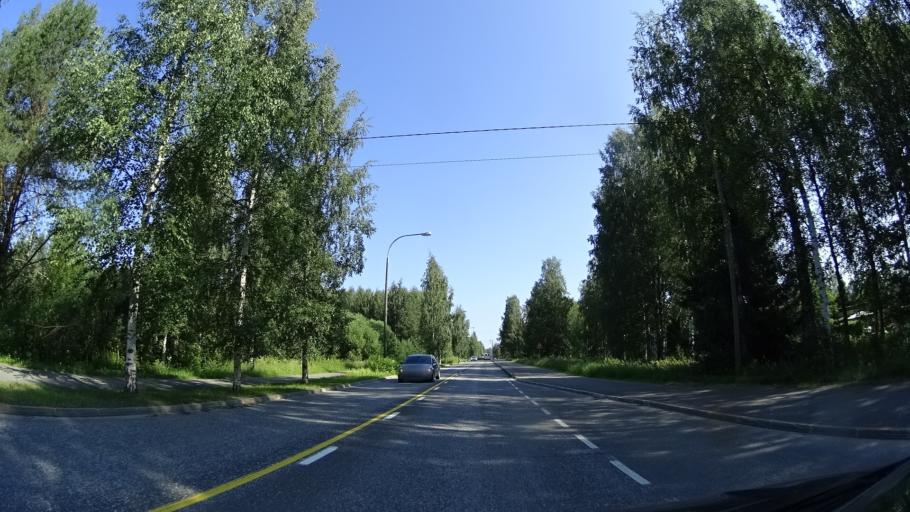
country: FI
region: North Karelia
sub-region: Joensuu
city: Juuka
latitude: 63.2359
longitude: 29.2465
